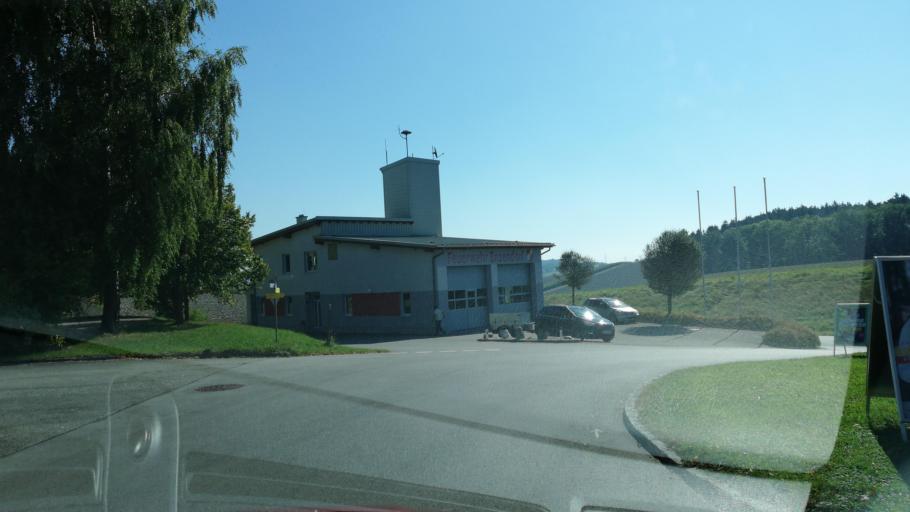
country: AT
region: Upper Austria
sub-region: Politischer Bezirk Grieskirchen
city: Grieskirchen
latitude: 48.2037
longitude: 13.8228
